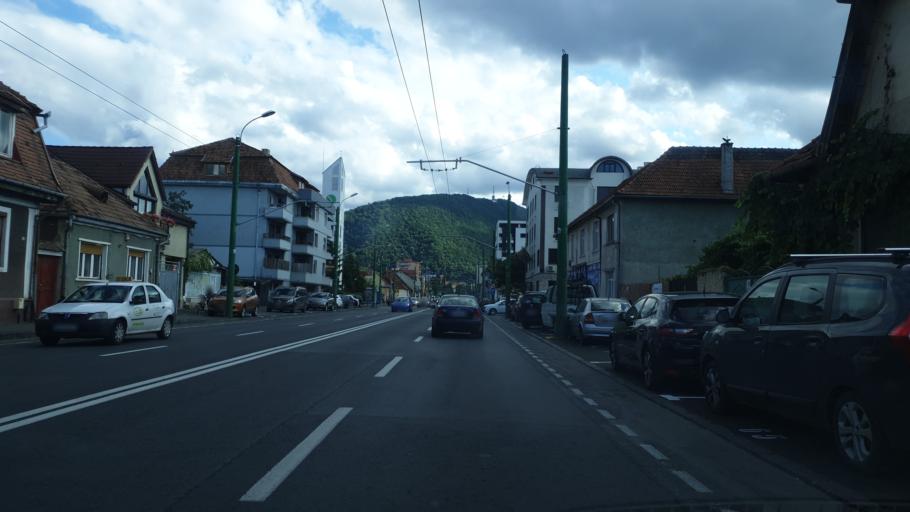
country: RO
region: Brasov
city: Brasov
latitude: 45.6581
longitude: 25.6065
